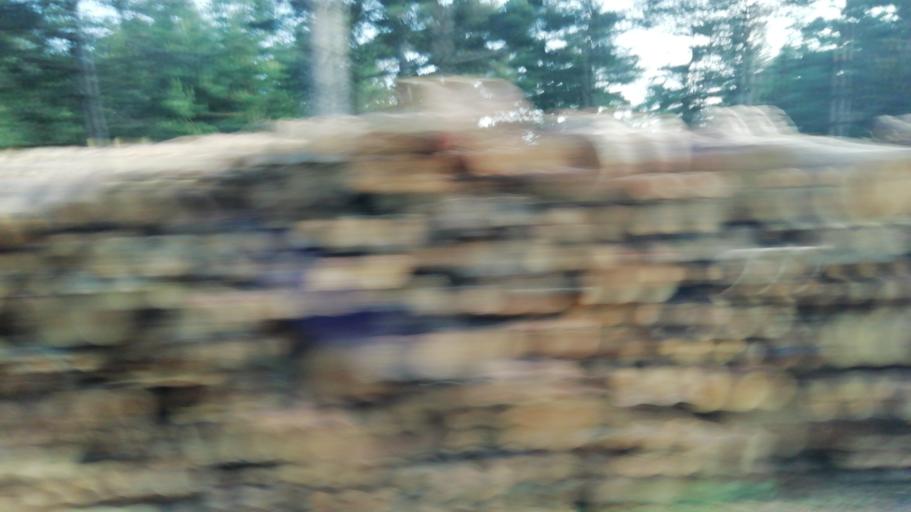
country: TR
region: Karabuk
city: Eskipazar
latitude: 41.0455
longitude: 32.5547
